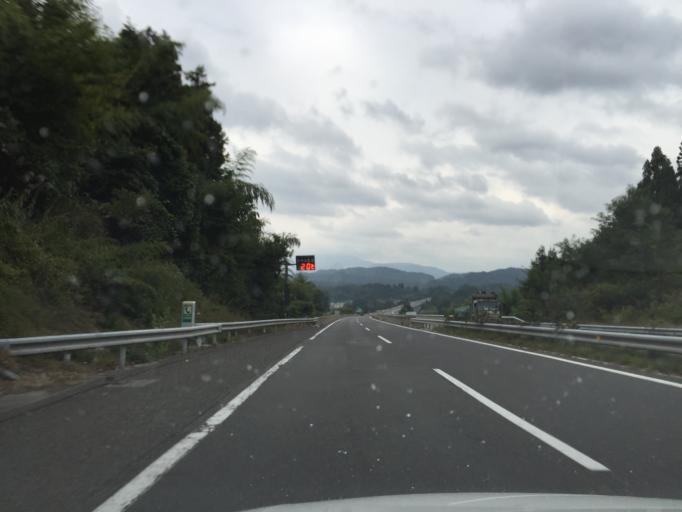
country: JP
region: Fukushima
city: Funehikimachi-funehiki
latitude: 37.3970
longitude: 140.5801
